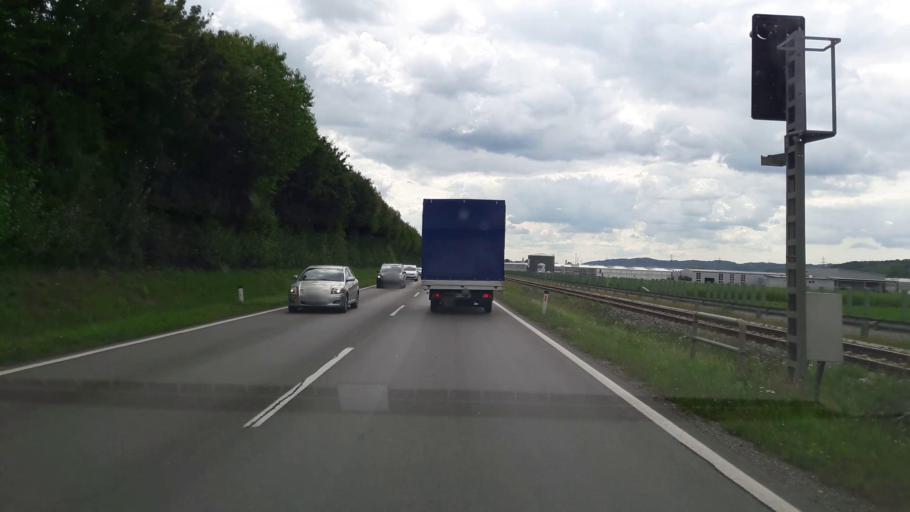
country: AT
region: Styria
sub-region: Politischer Bezirk Weiz
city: Sankt Ruprecht an der Raab
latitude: 47.1331
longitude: 15.6841
